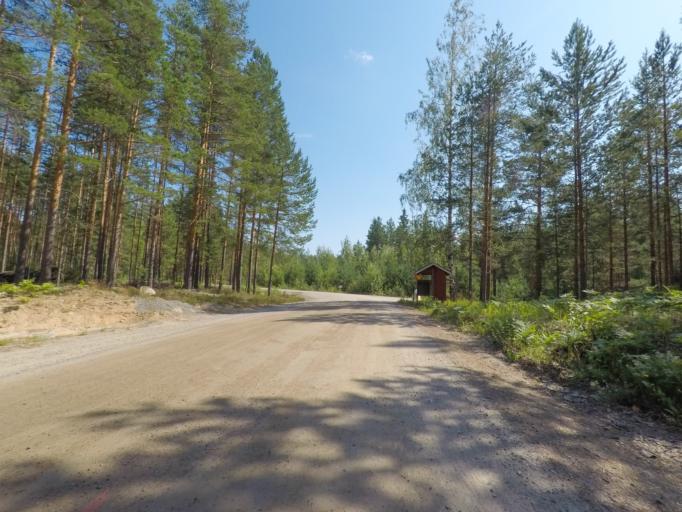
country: FI
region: Southern Savonia
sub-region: Mikkeli
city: Puumala
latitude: 61.4053
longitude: 28.0478
